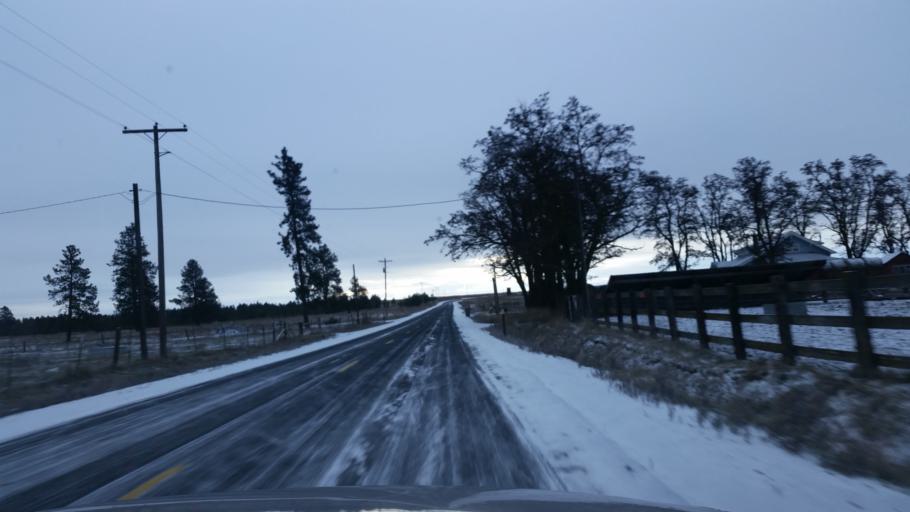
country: US
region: Washington
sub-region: Spokane County
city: Cheney
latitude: 47.4168
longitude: -117.4937
